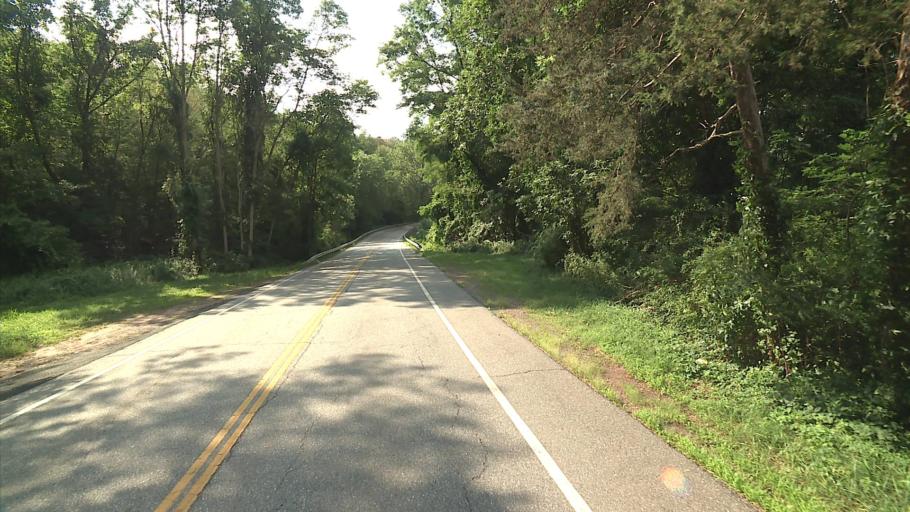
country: US
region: Connecticut
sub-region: Middlesex County
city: East Haddam
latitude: 41.4692
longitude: -72.4663
